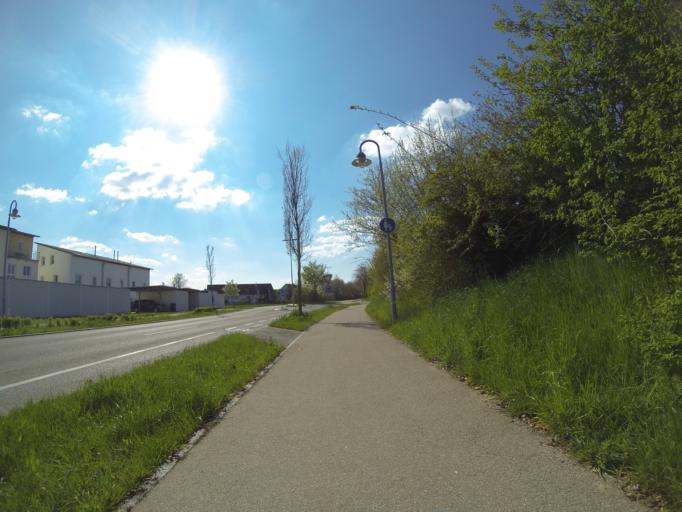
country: DE
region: Baden-Wuerttemberg
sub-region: Tuebingen Region
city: Laupheim
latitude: 48.2276
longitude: 9.8982
